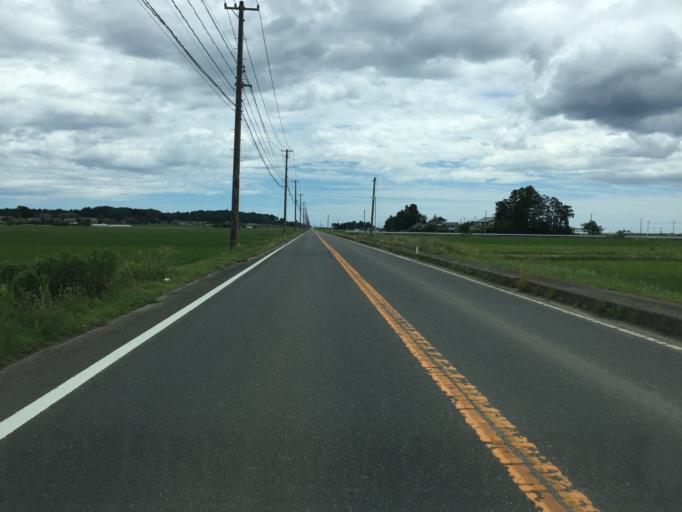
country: JP
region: Fukushima
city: Namie
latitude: 37.7067
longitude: 140.9730
